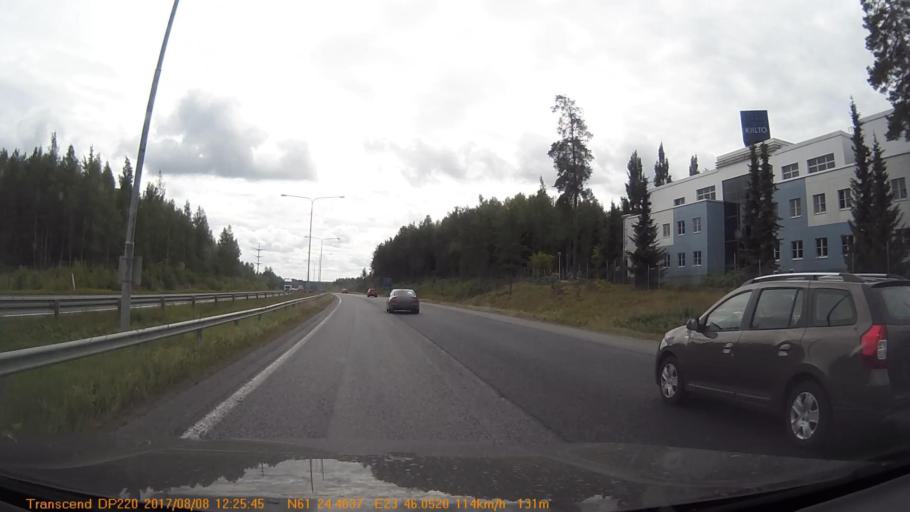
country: FI
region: Pirkanmaa
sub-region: Tampere
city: Lempaeaelae
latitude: 61.4067
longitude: 23.7675
